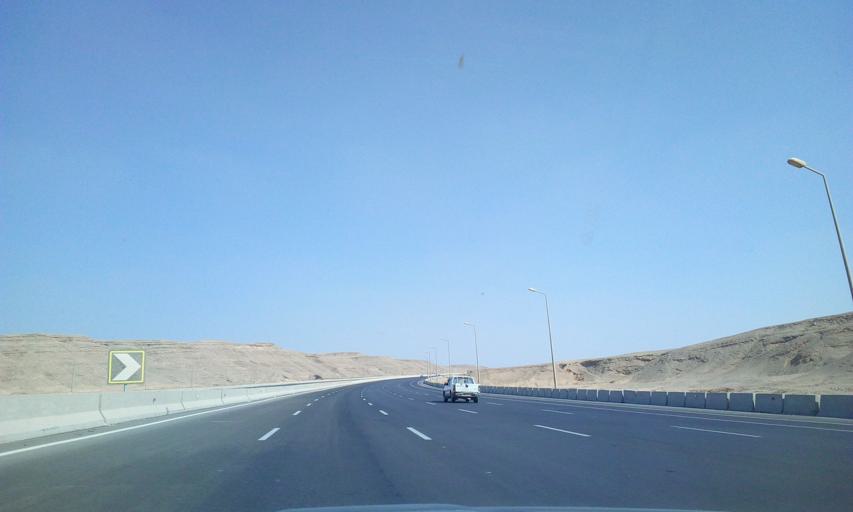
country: EG
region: As Suways
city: Ain Sukhna
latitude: 29.7565
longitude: 32.0203
